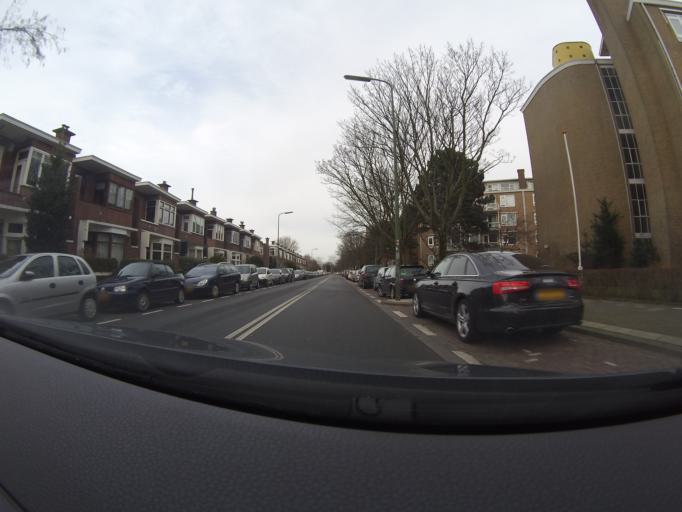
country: NL
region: South Holland
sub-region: Gemeente Den Haag
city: Scheveningen
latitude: 52.0839
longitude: 4.2686
